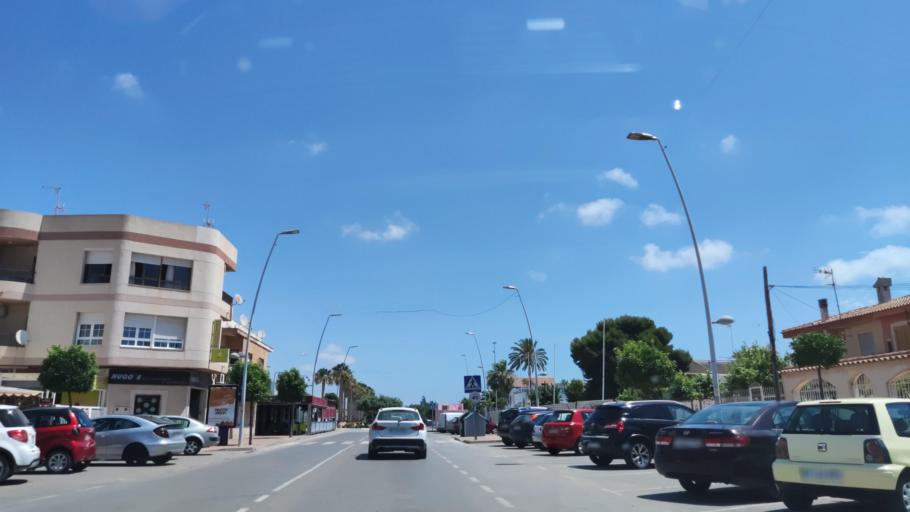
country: ES
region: Murcia
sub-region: Murcia
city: Los Alcazares
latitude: 37.7582
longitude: -0.8390
